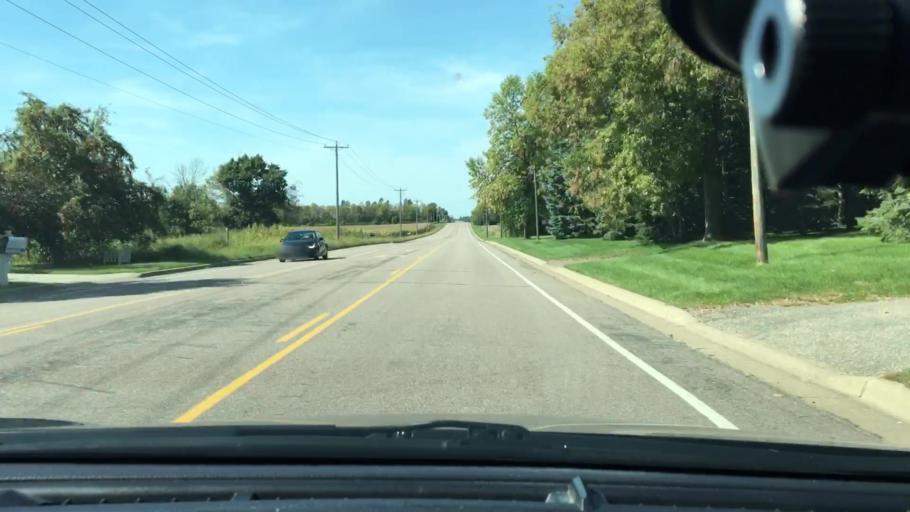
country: US
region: Minnesota
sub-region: Wright County
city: Saint Michael
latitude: 45.1954
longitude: -93.6684
